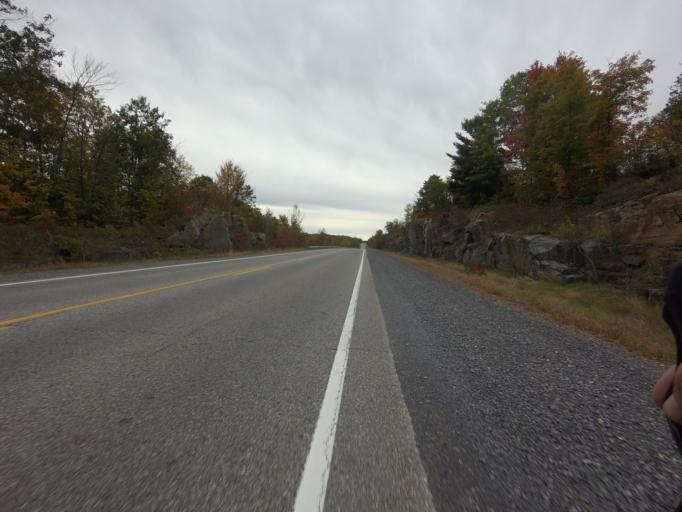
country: CA
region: Ontario
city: Gananoque
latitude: 44.4008
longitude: -76.3135
